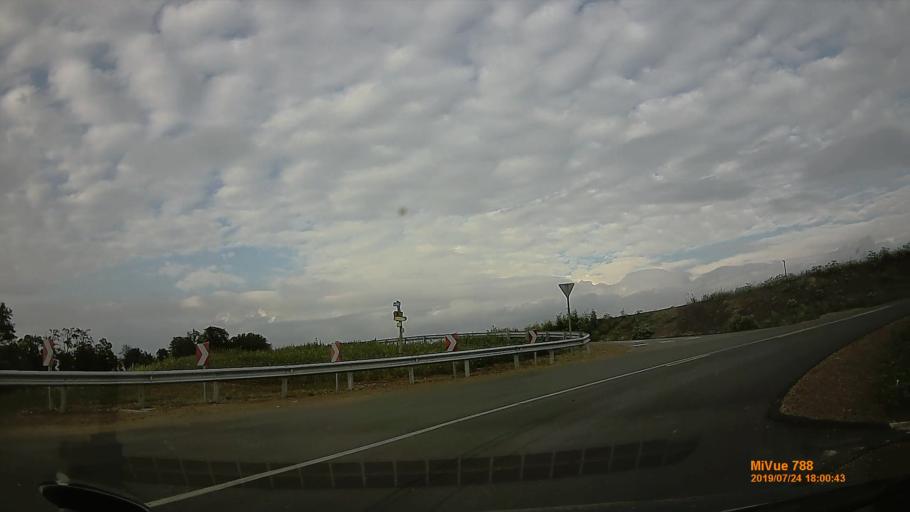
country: HU
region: Borsod-Abauj-Zemplen
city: Encs
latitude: 48.3165
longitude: 21.1655
